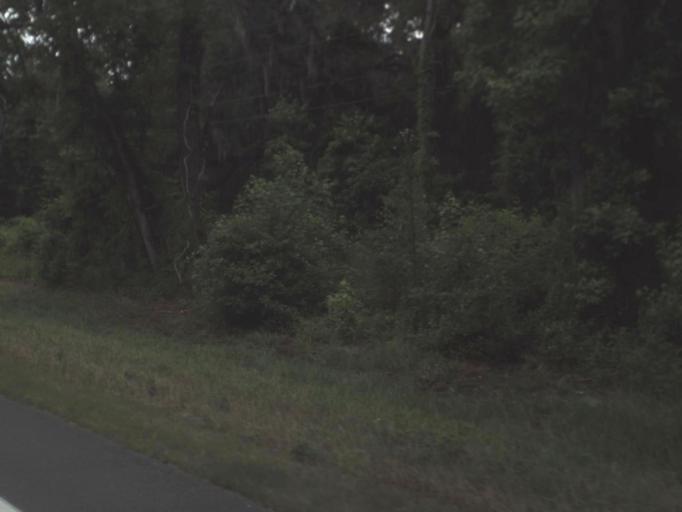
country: US
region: Florida
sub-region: Alachua County
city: Gainesville
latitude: 29.5613
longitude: -82.3919
